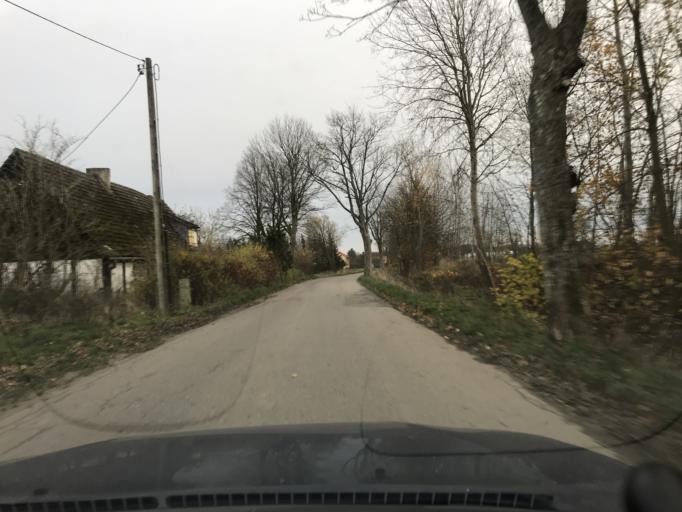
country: PL
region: Pomeranian Voivodeship
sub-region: Powiat slupski
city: Kobylnica
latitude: 54.4448
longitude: 16.8886
